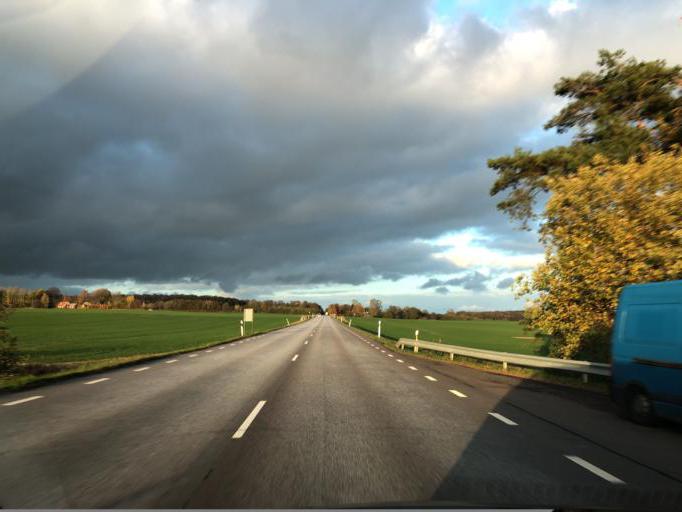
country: SE
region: Skane
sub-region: Svalovs Kommun
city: Svaloev
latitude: 55.9366
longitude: 13.2182
